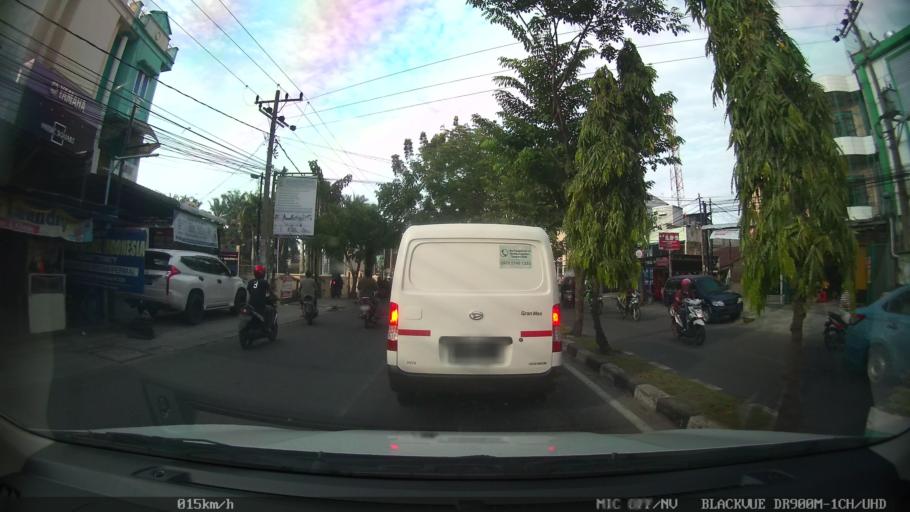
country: ID
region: North Sumatra
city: Sunggal
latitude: 3.5635
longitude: 98.6390
